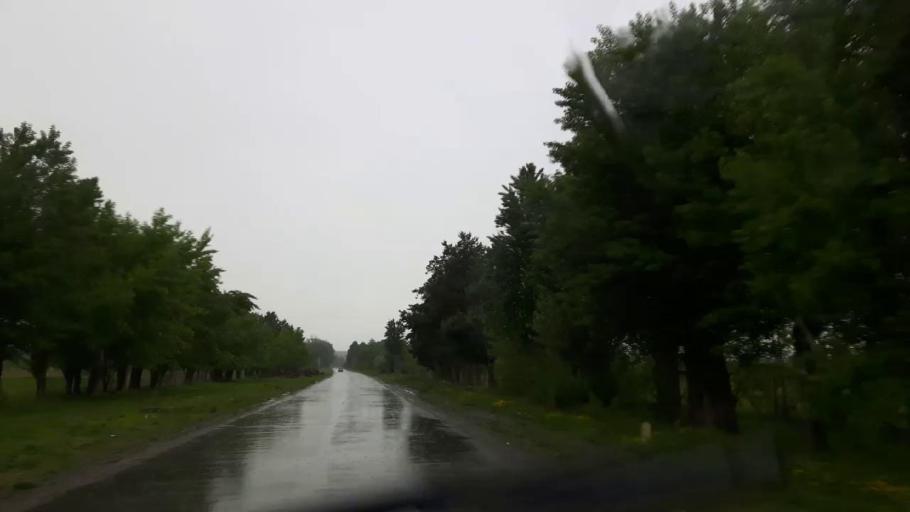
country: GE
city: Agara
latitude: 42.0111
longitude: 43.8594
